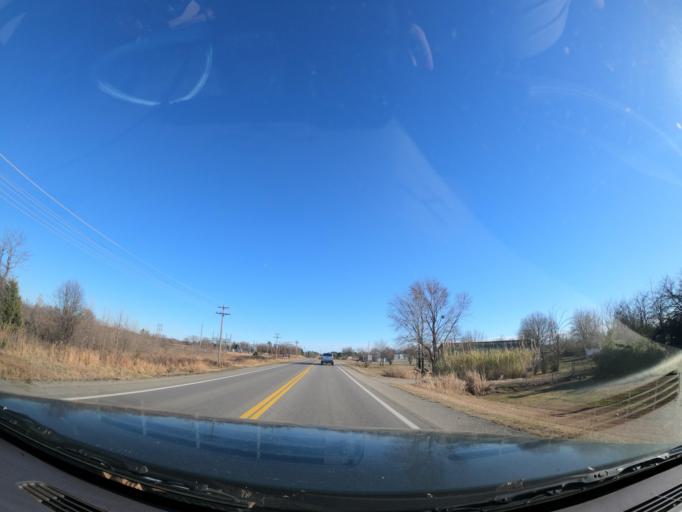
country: US
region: Oklahoma
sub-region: Pittsburg County
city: Longtown
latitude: 35.2355
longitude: -95.4642
